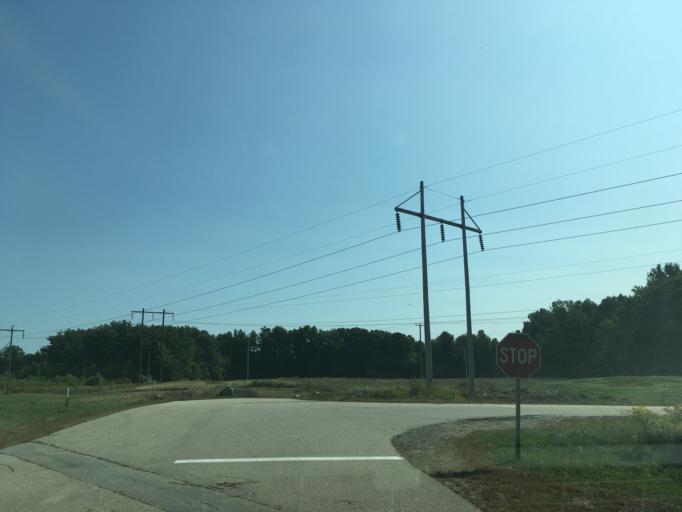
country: US
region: New Hampshire
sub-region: Rockingham County
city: Stratham Station
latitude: 43.0100
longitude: -70.8851
